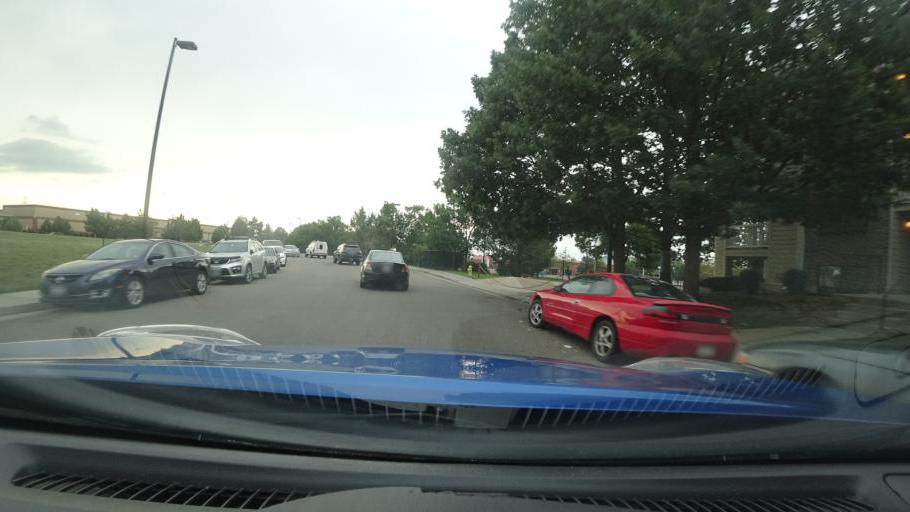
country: US
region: Colorado
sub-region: Adams County
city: Aurora
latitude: 39.7009
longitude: -104.8241
